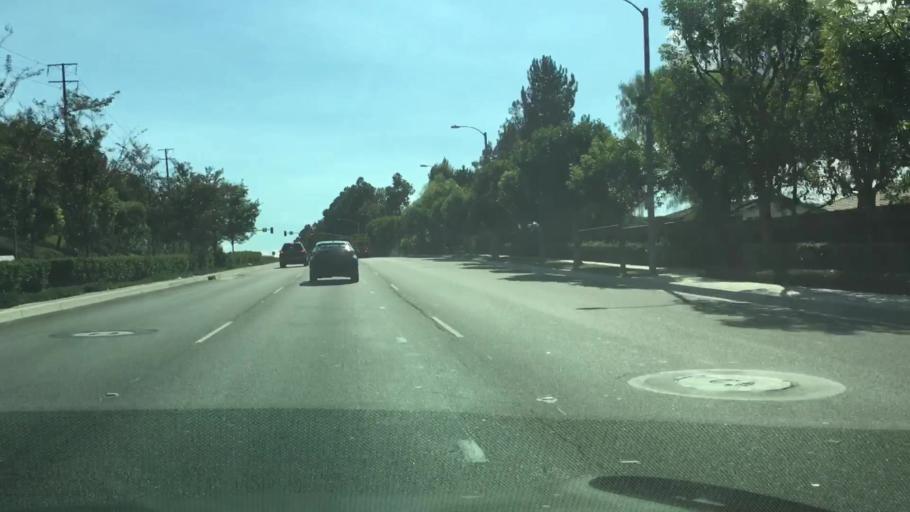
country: US
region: California
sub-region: Los Angeles County
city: East La Mirada
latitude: 33.9045
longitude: -117.9816
